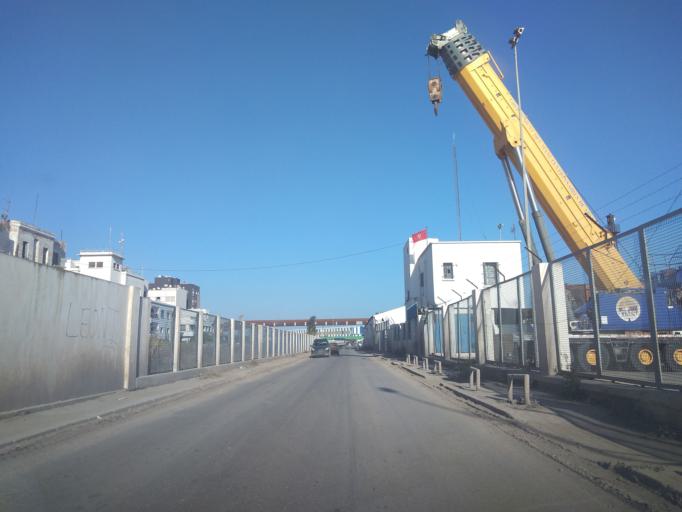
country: TN
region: Safaqis
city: Sfax
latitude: 34.7308
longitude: 10.7673
